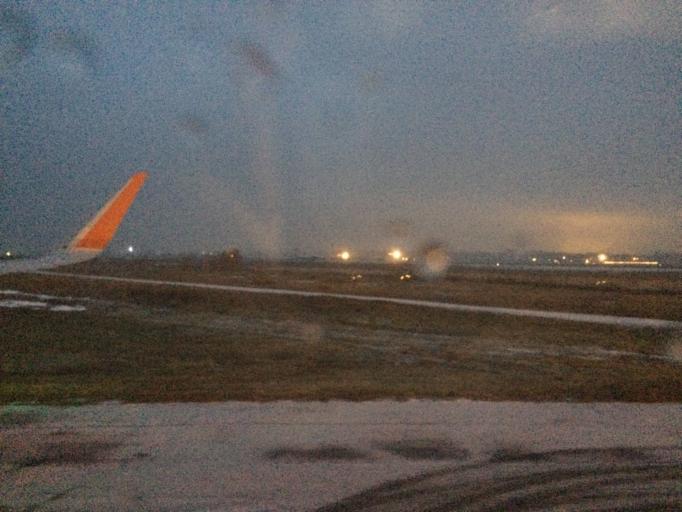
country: RU
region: Novosibirsk
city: Ob'
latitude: 55.0112
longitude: 82.6747
